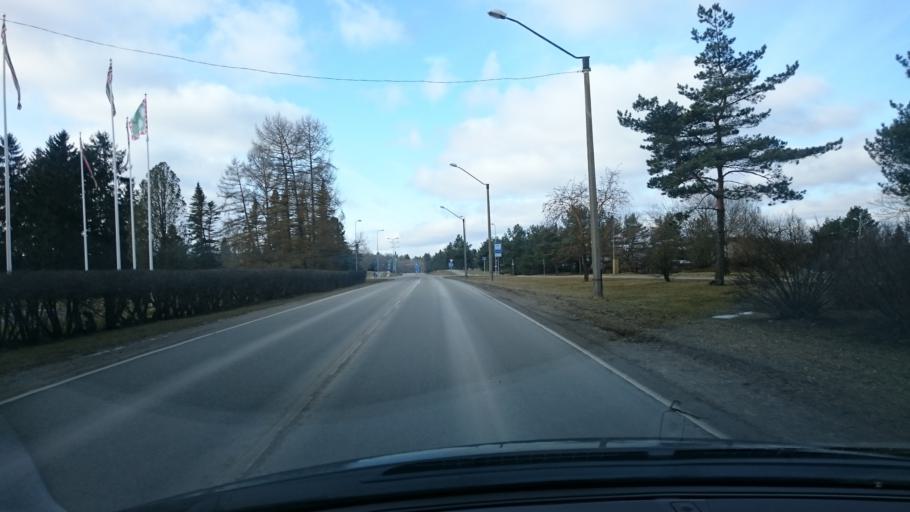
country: EE
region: Harju
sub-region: Saku vald
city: Saku
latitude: 59.3005
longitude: 24.6595
